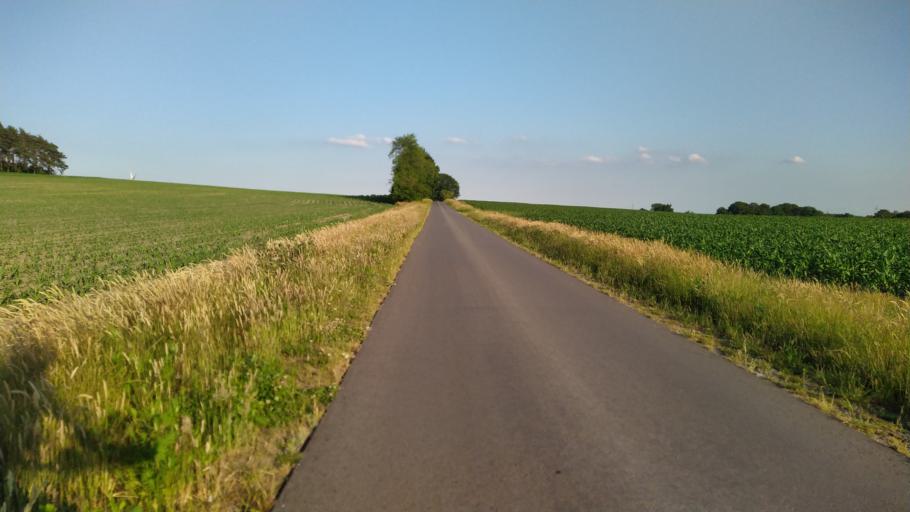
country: DE
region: Lower Saxony
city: Alfstedt
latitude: 53.5691
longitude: 9.0246
